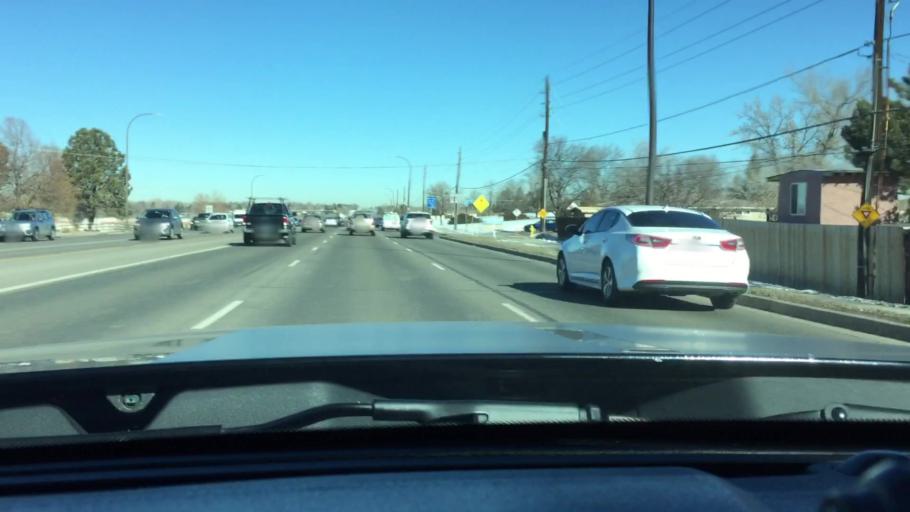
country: US
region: Colorado
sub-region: Jefferson County
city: Arvada
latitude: 39.8325
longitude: -105.0810
